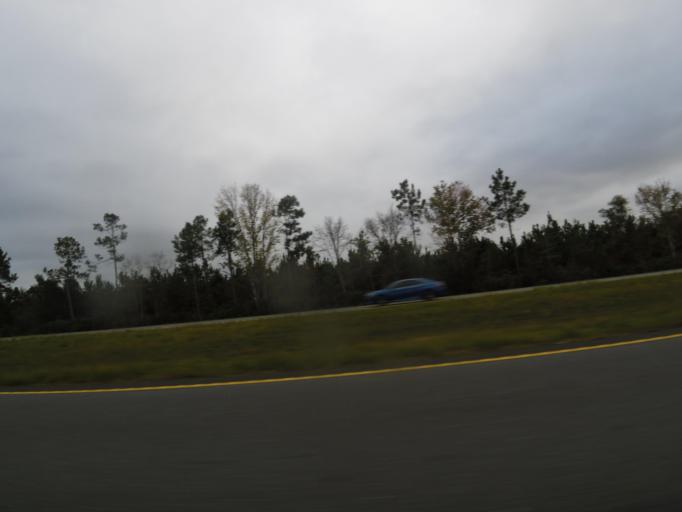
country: US
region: Georgia
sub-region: Charlton County
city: Folkston
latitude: 30.8835
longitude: -82.0389
